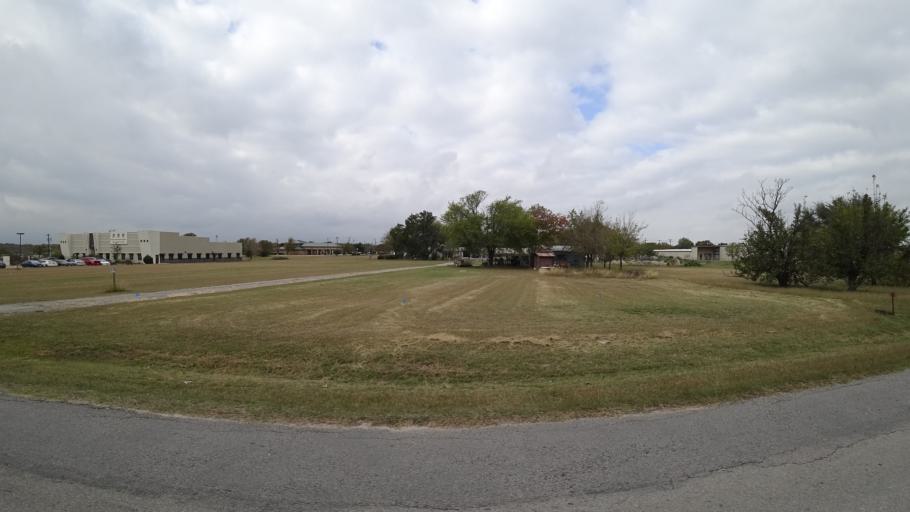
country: US
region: Texas
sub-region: Travis County
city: Pflugerville
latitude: 30.4411
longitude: -97.6081
